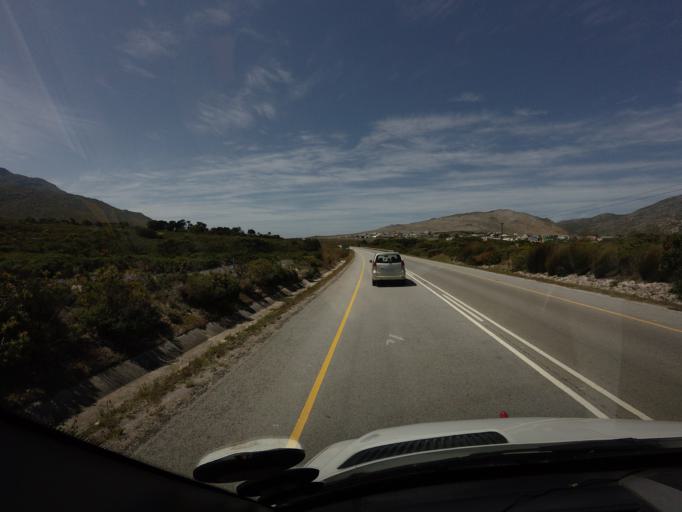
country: ZA
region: Western Cape
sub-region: Overberg District Municipality
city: Grabouw
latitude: -34.3377
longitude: 18.8420
